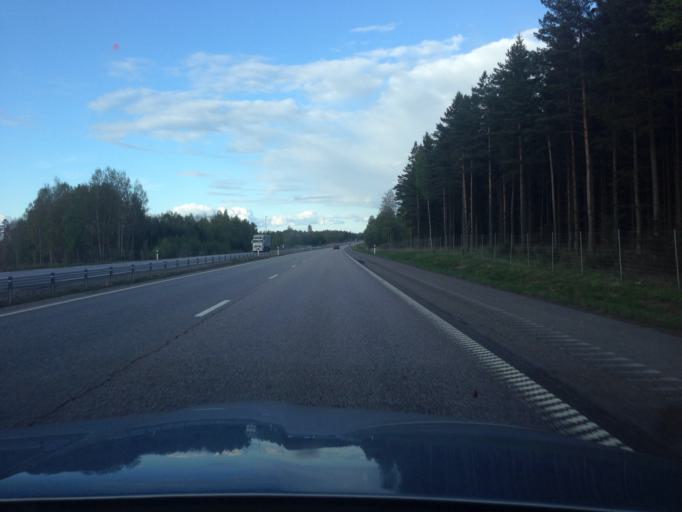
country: SE
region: OEstergoetland
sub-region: Mjolby Kommun
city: Mjolby
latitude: 58.3510
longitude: 15.2006
